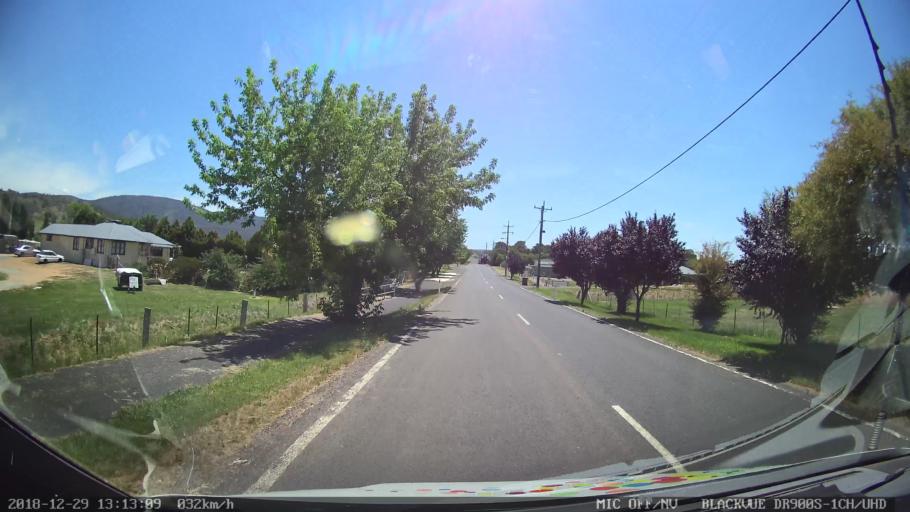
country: AU
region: Australian Capital Territory
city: Macarthur
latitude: -35.7083
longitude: 149.1642
